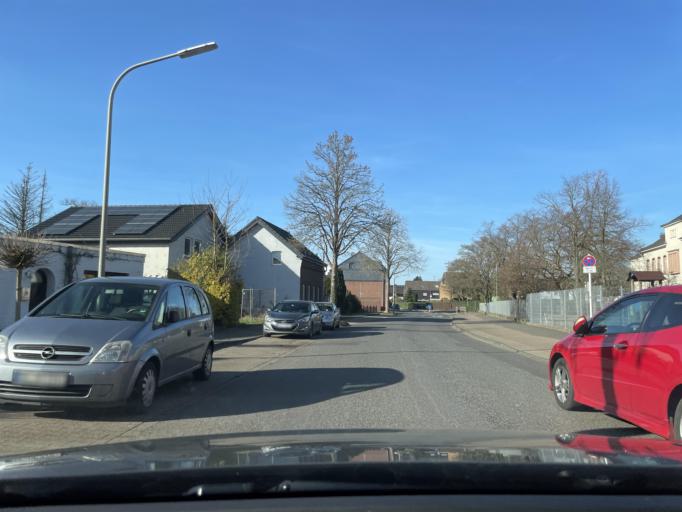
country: DE
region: North Rhine-Westphalia
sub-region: Regierungsbezirk Dusseldorf
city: Monchengladbach
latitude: 51.2198
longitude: 6.4691
